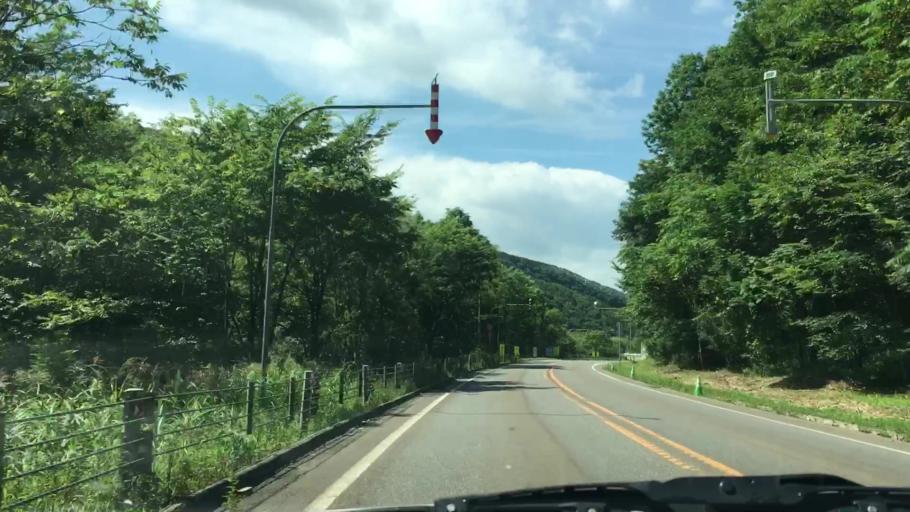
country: JP
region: Hokkaido
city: Otofuke
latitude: 43.2530
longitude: 143.4641
